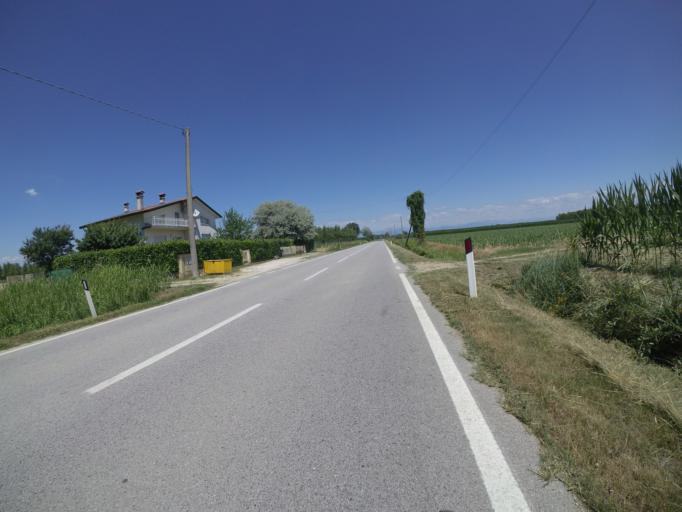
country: IT
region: Friuli Venezia Giulia
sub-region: Provincia di Udine
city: Rivignano
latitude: 45.8887
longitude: 13.0770
